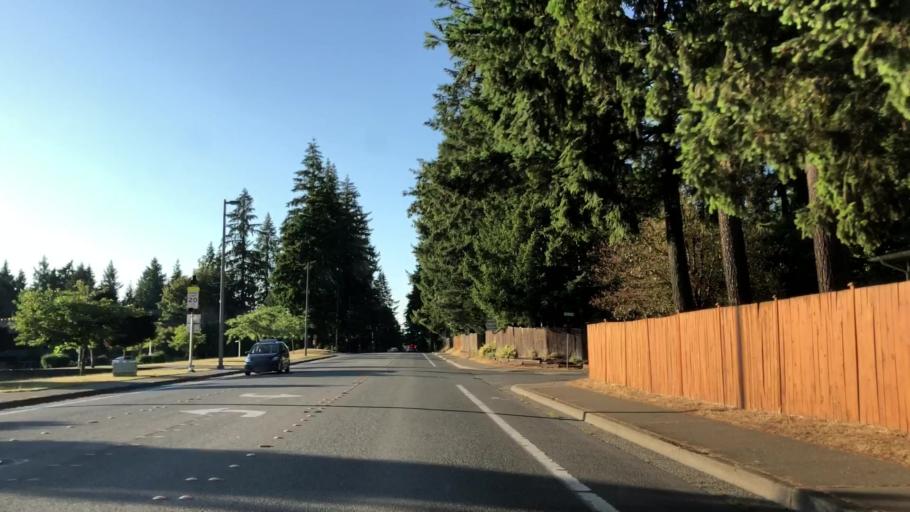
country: US
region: Washington
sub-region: King County
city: Redmond
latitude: 47.6910
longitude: -122.1180
